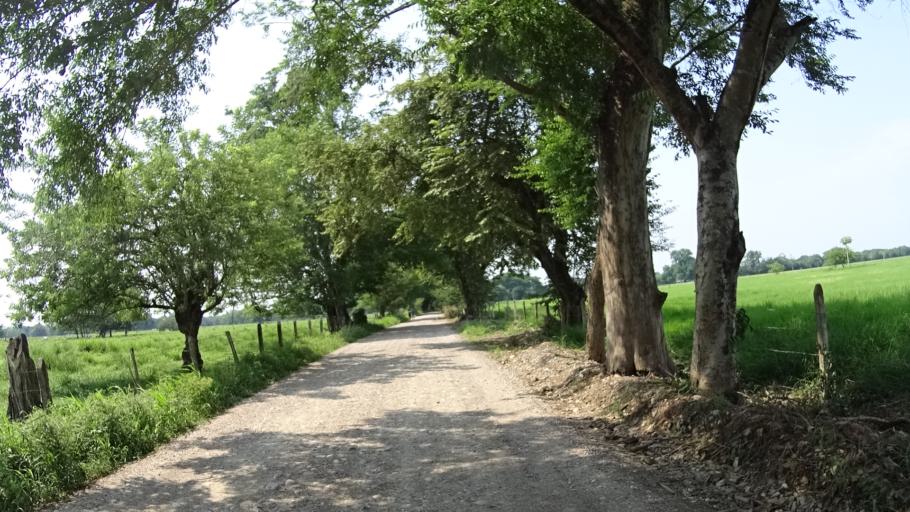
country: CO
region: Cundinamarca
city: Puerto Salgar
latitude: 5.5195
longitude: -74.6879
